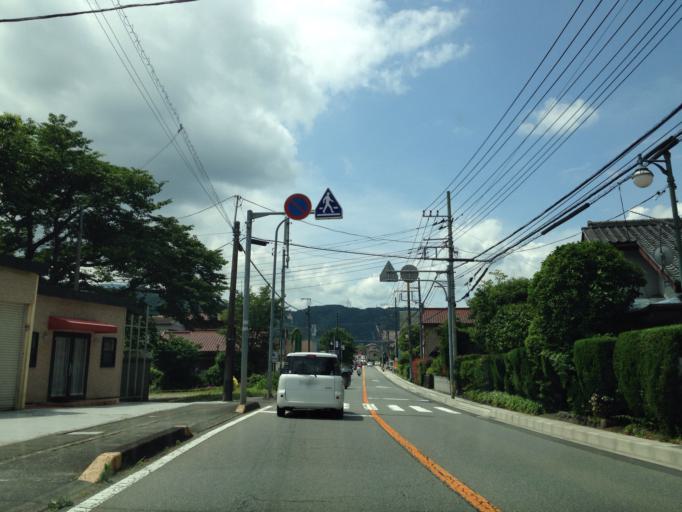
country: JP
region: Shizuoka
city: Heda
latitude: 34.9322
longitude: 138.9335
